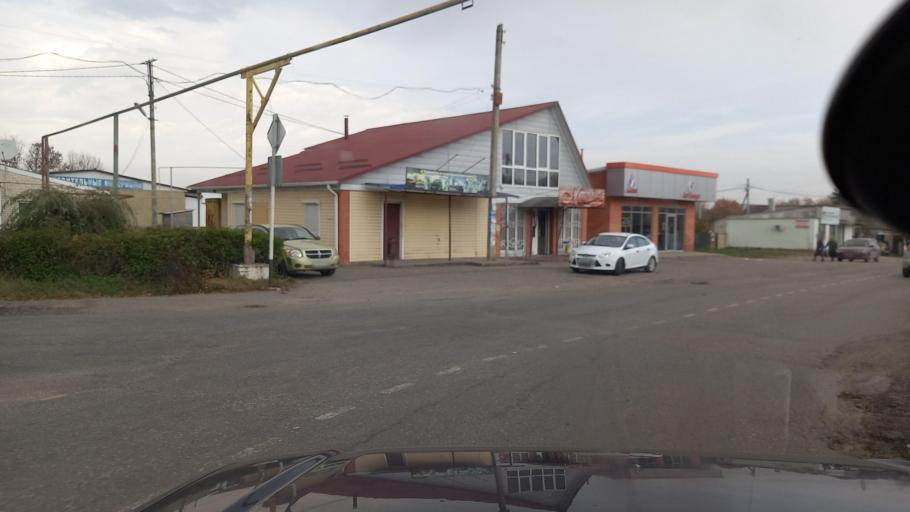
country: RU
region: Krasnodarskiy
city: Shedok
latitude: 44.1713
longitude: 40.8378
